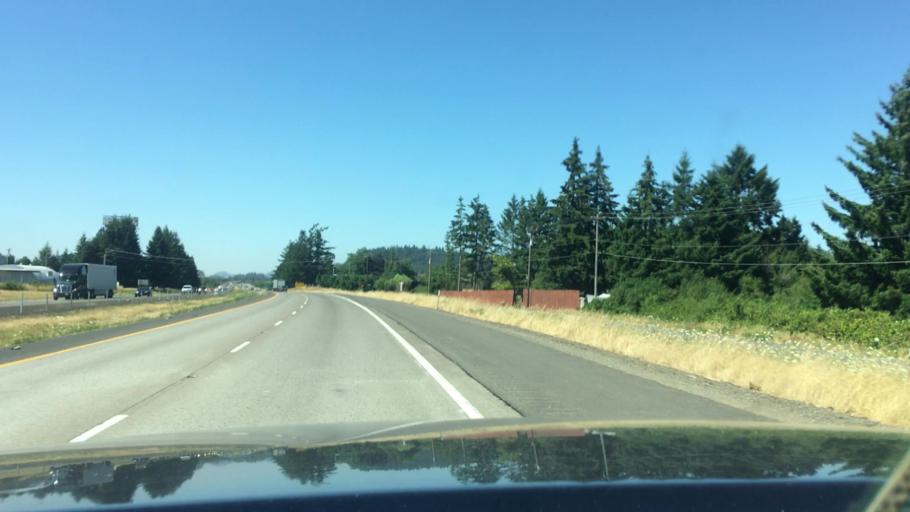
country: US
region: Oregon
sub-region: Lane County
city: Creswell
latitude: 43.9443
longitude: -123.0086
